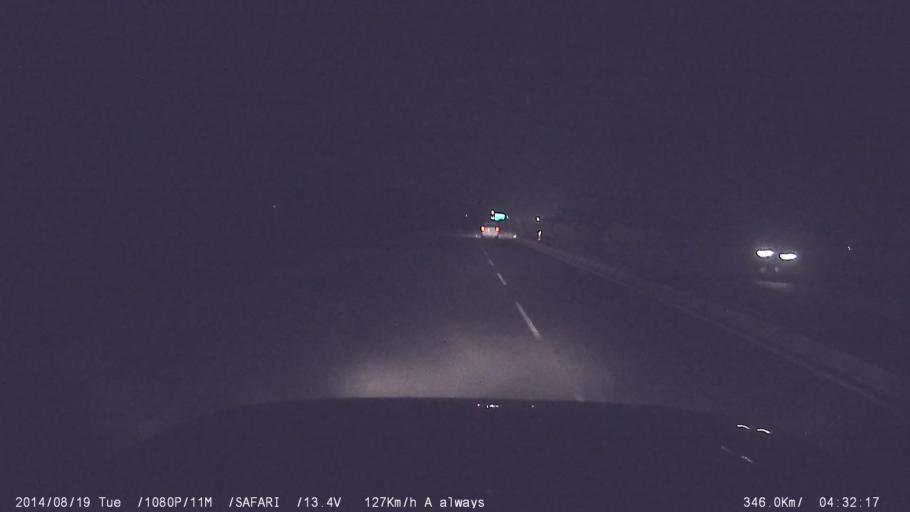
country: IN
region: Tamil Nadu
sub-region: Erode
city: Perundurai
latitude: 11.2908
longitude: 77.5708
